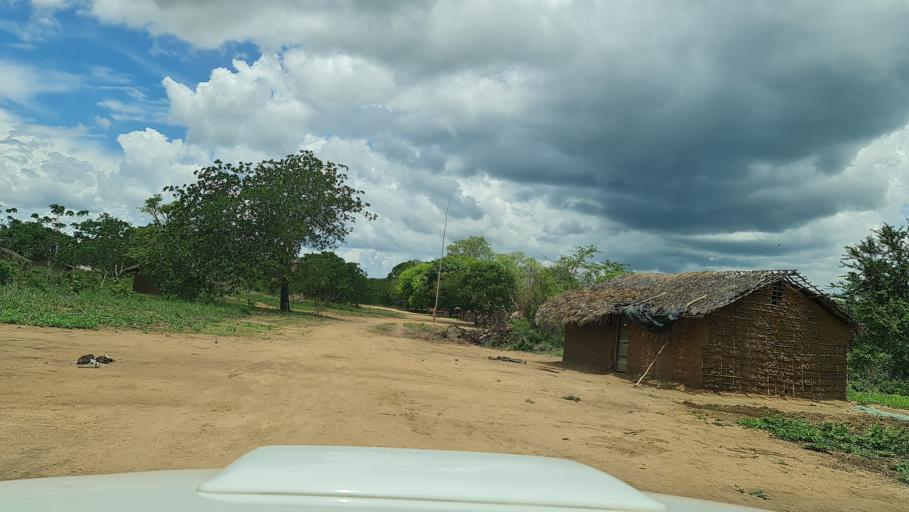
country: MZ
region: Nampula
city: Ilha de Mocambique
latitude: -15.5169
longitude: 40.2020
